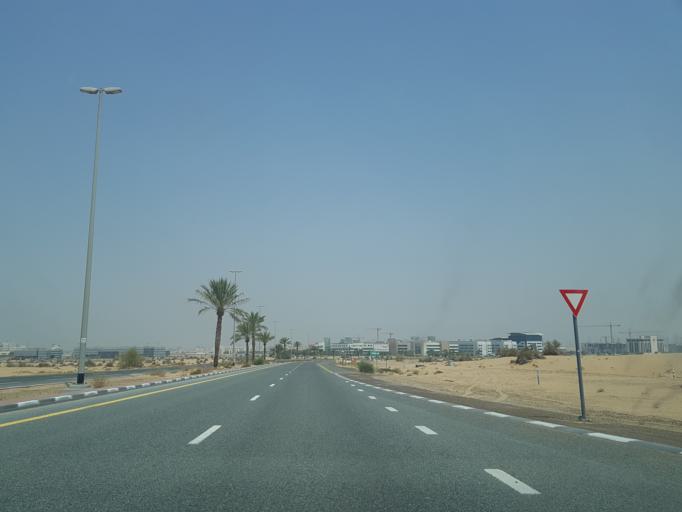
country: AE
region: Ash Shariqah
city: Sharjah
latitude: 25.1175
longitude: 55.4292
